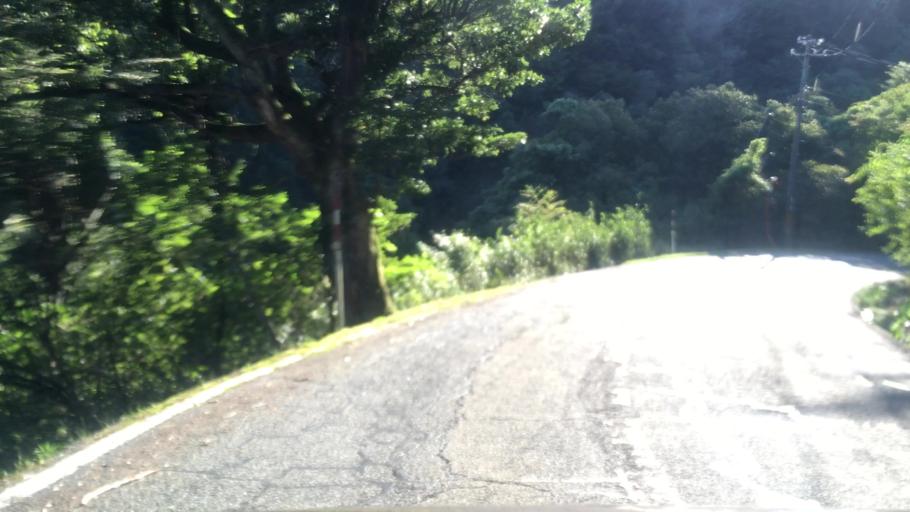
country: JP
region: Hyogo
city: Toyooka
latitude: 35.6201
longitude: 134.8709
